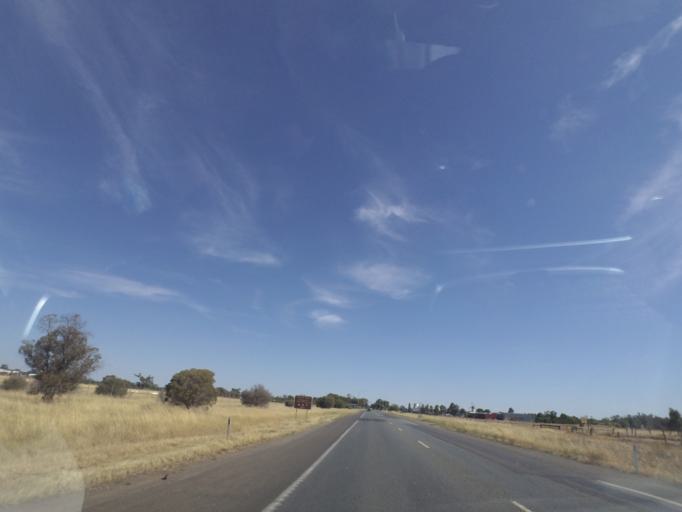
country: AU
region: Victoria
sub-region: Greater Shepparton
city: Shepparton
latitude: -36.4322
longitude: 145.3888
